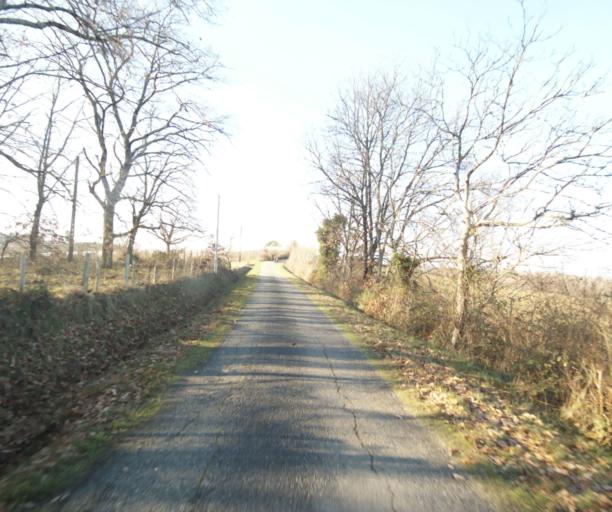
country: FR
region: Midi-Pyrenees
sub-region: Departement du Tarn-et-Garonne
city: Moissac
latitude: 44.1430
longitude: 1.0689
